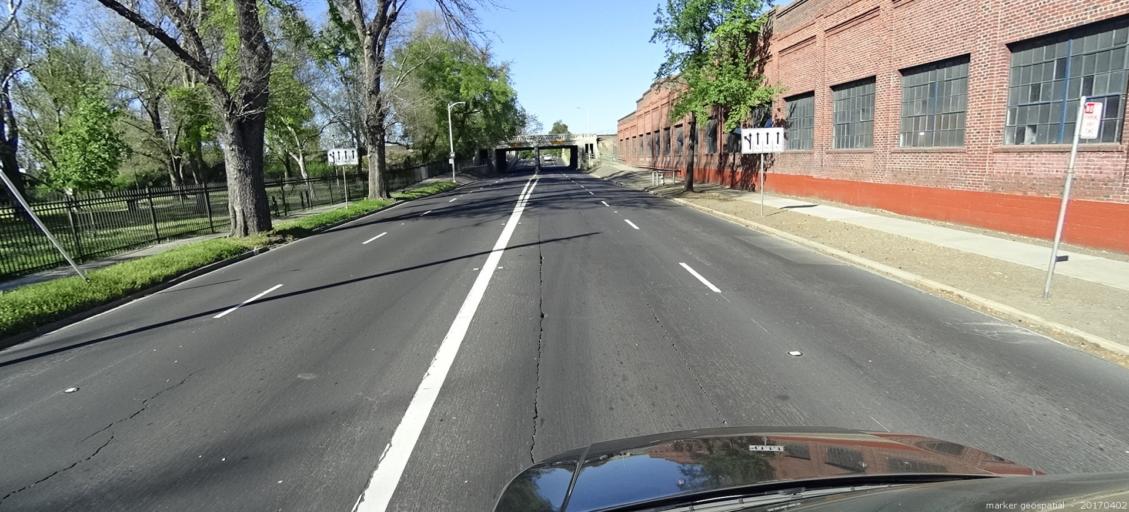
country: US
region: California
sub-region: Sacramento County
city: Sacramento
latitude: 38.5859
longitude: -121.4819
